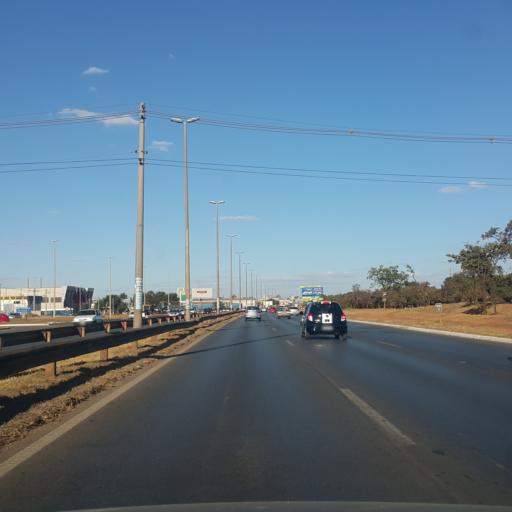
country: BR
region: Federal District
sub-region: Brasilia
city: Brasilia
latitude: -15.7873
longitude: -47.9900
